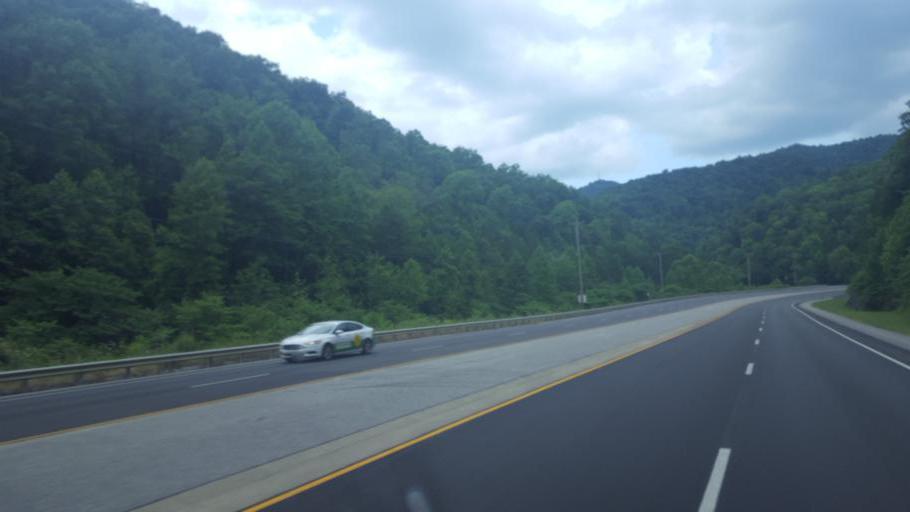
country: US
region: Kentucky
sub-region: Letcher County
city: Jenkins
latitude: 37.3035
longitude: -82.5443
